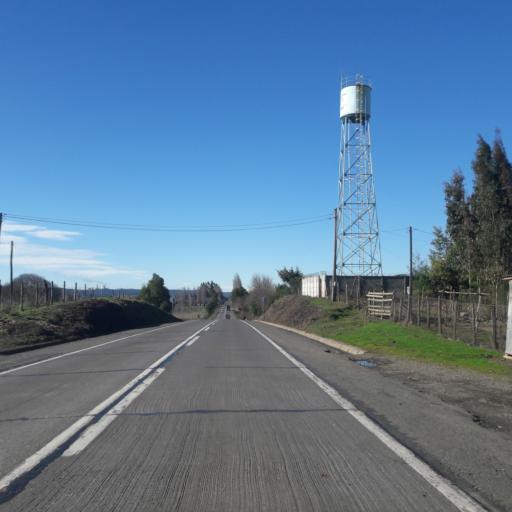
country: CL
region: Araucania
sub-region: Provincia de Malleco
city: Angol
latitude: -37.7671
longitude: -72.5584
